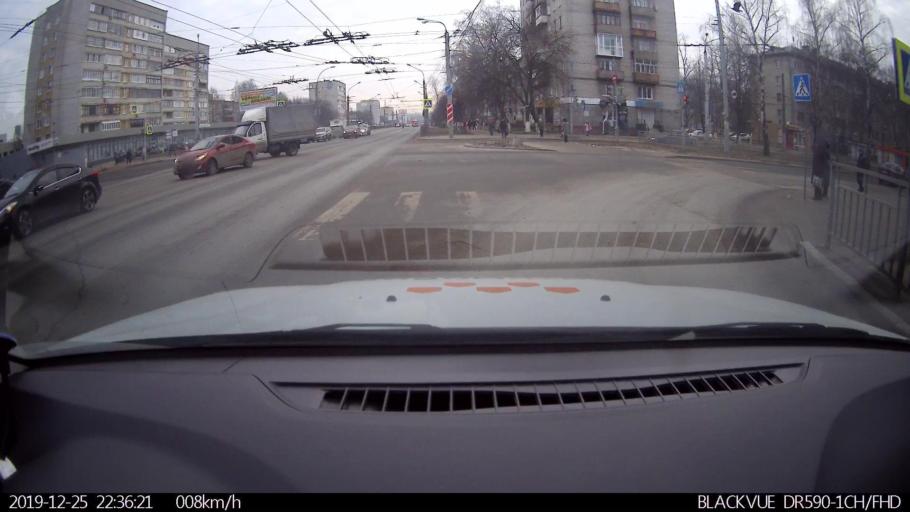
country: RU
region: Nizjnij Novgorod
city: Burevestnik
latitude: 56.2377
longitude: 43.8672
